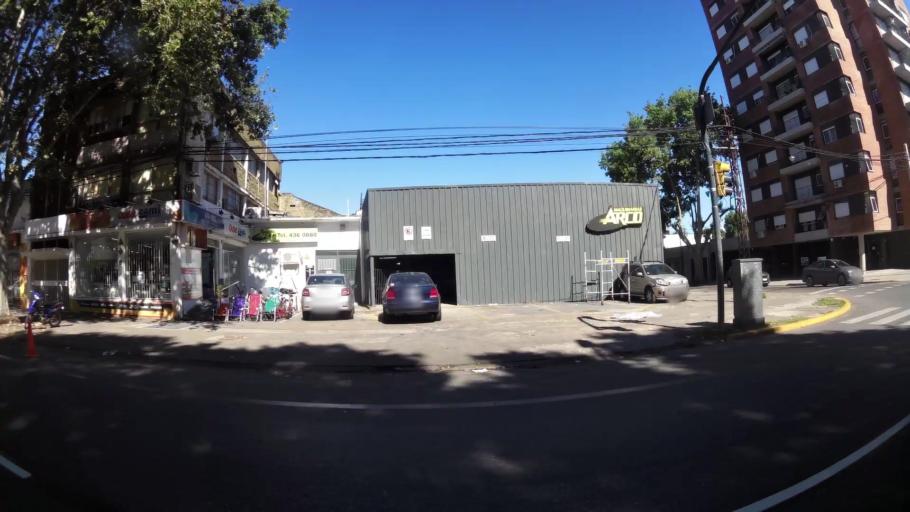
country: AR
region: Santa Fe
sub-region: Departamento de Rosario
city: Rosario
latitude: -32.9489
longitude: -60.6817
